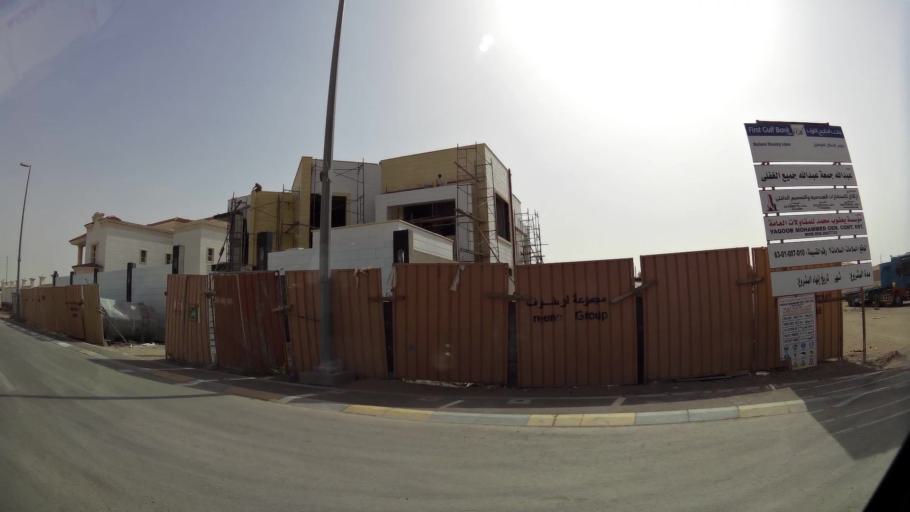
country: AE
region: Abu Dhabi
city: Al Ain
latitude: 24.2077
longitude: 55.5760
